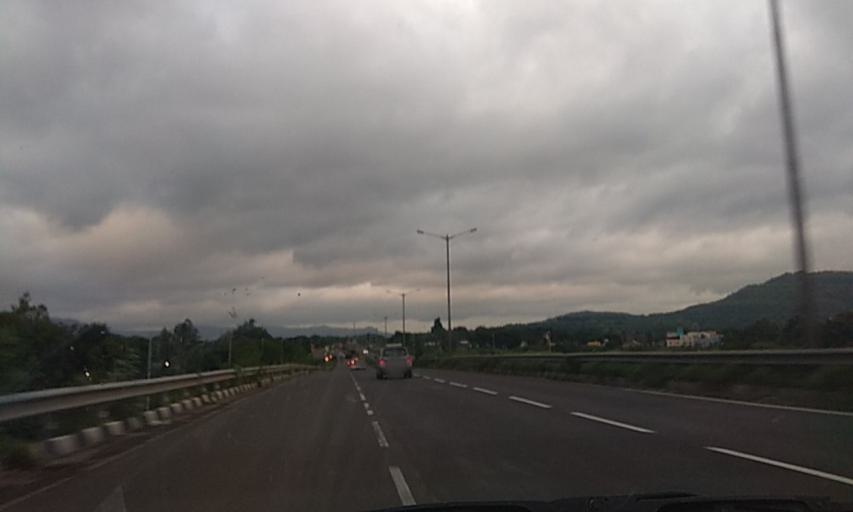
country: IN
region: Maharashtra
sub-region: Satara Division
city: Wai
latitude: 17.9042
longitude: 73.9722
